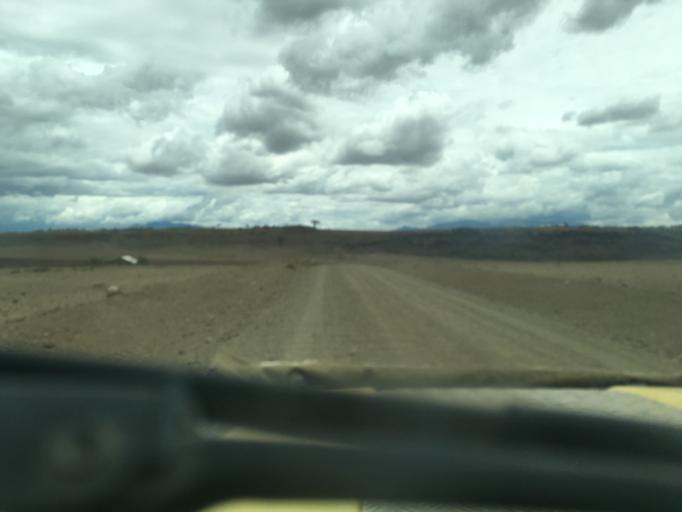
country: TZ
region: Arusha
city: Mto wa Mbu
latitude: -3.2117
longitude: 35.9507
